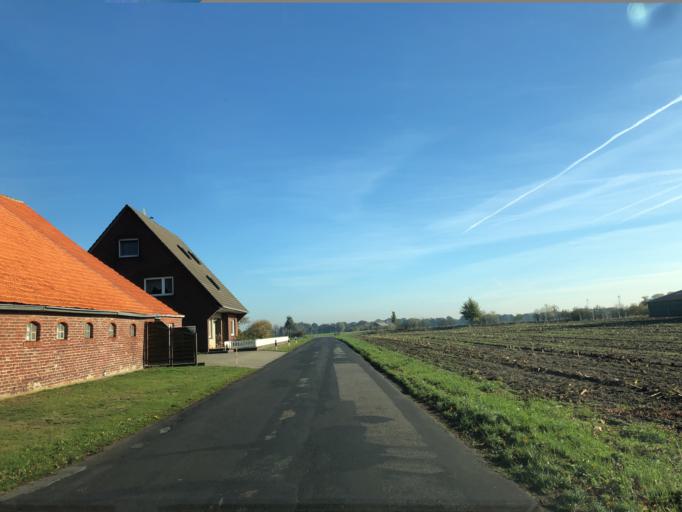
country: DE
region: Lower Saxony
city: Lehe
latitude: 53.0315
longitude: 7.3222
